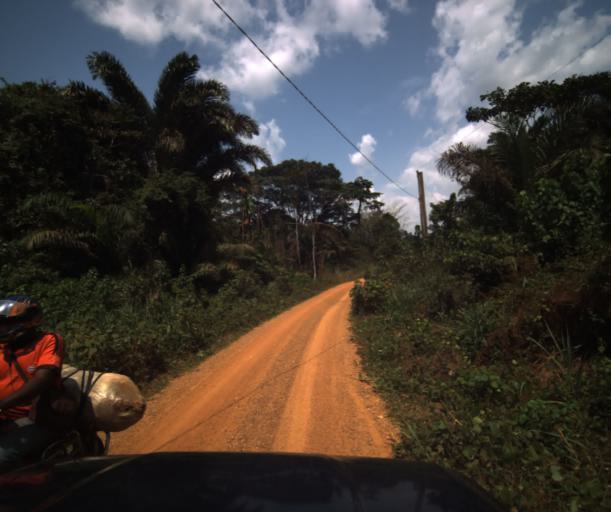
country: CM
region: Centre
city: Eseka
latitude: 3.5409
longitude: 11.0119
